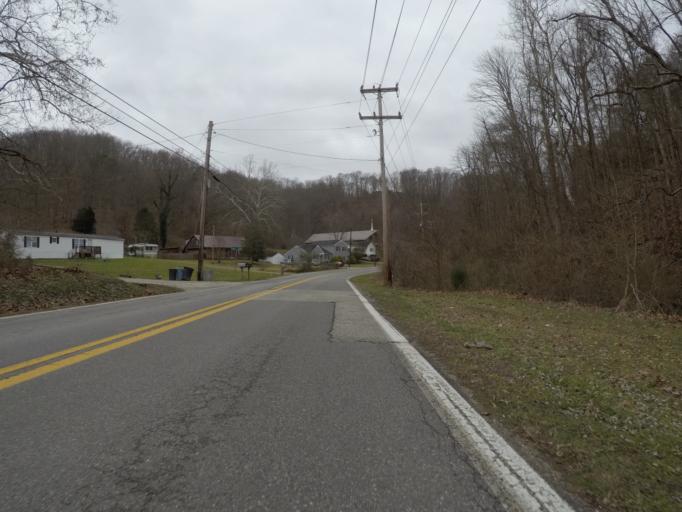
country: US
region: West Virginia
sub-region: Cabell County
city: Barboursville
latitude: 38.4545
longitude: -82.2978
